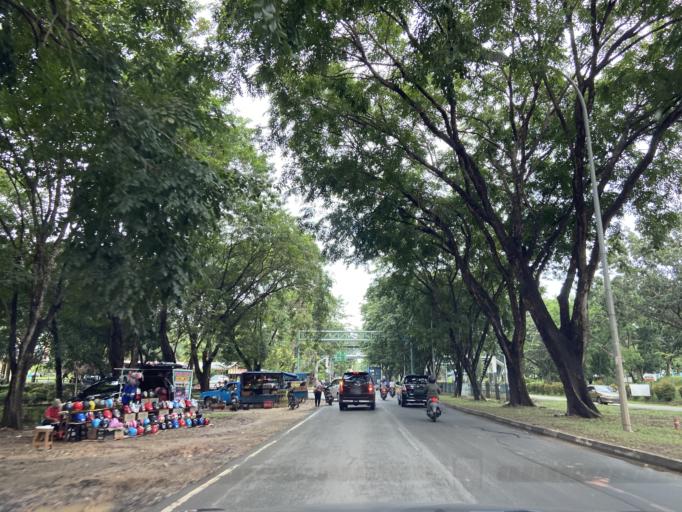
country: SG
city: Singapore
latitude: 1.1074
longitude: 103.9525
